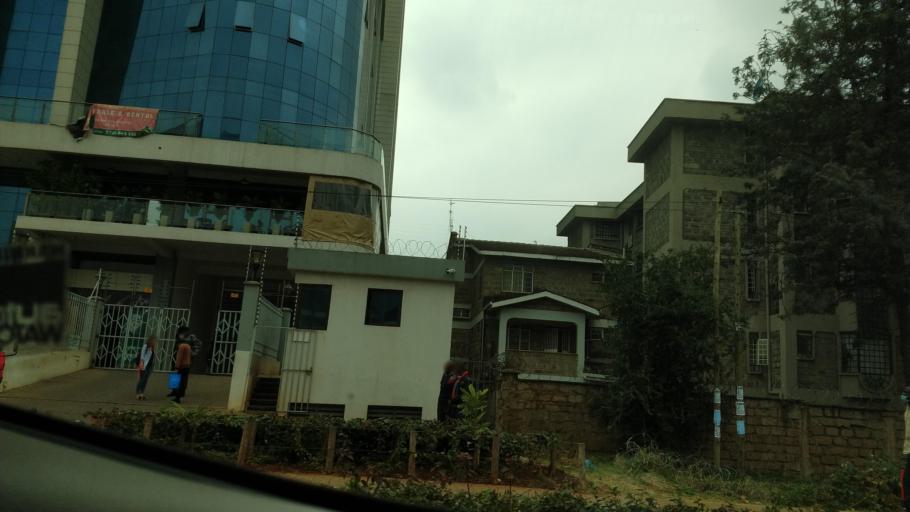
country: KE
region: Nairobi Area
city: Nairobi
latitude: -1.2998
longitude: 36.7812
